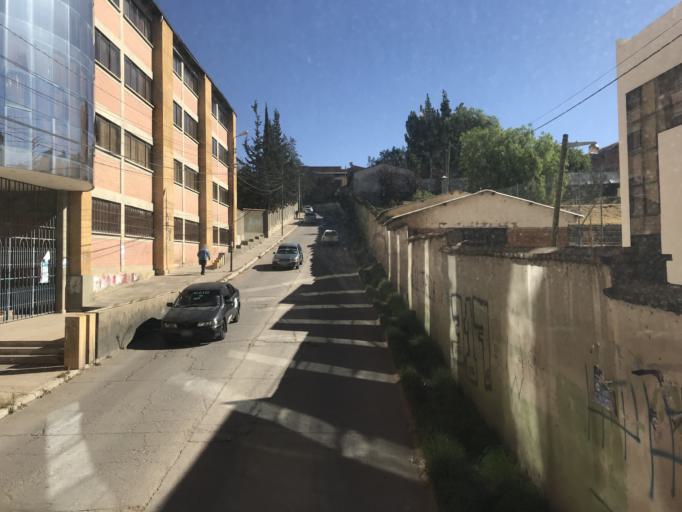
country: BO
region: Chuquisaca
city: Sucre
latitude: -19.0414
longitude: -65.2461
